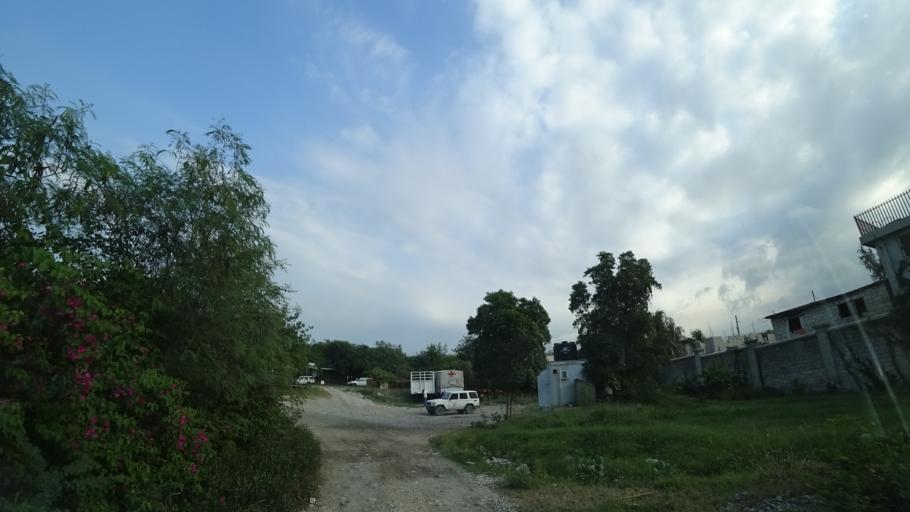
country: HT
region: Ouest
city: Delmas 73
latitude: 18.5709
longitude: -72.2969
